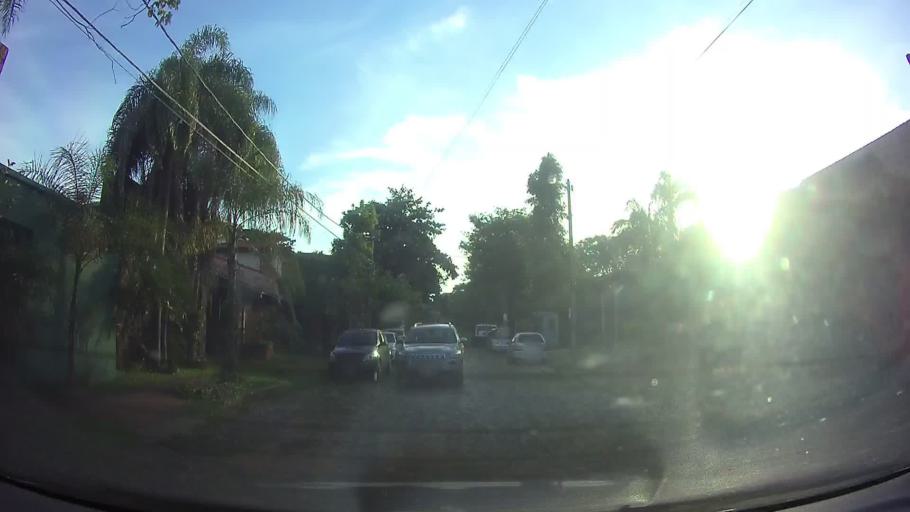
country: PY
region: Asuncion
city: Asuncion
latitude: -25.2734
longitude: -57.5705
